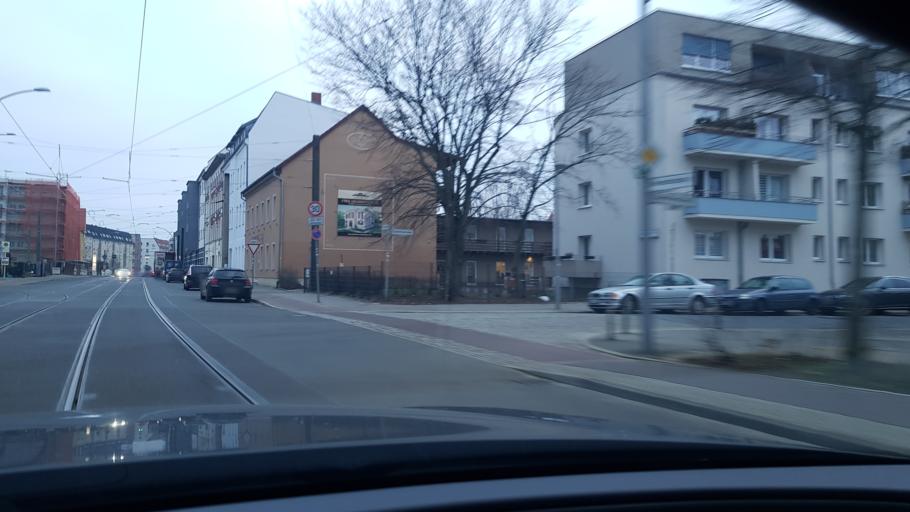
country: DE
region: Berlin
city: Berlin Koepenick
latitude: 52.4385
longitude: 13.5820
